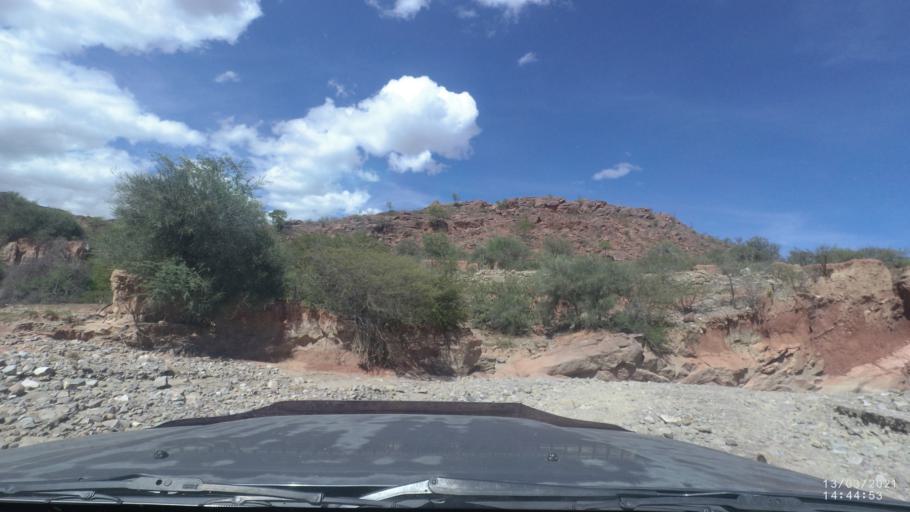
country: BO
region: Cochabamba
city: Cliza
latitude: -17.9424
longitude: -65.8602
